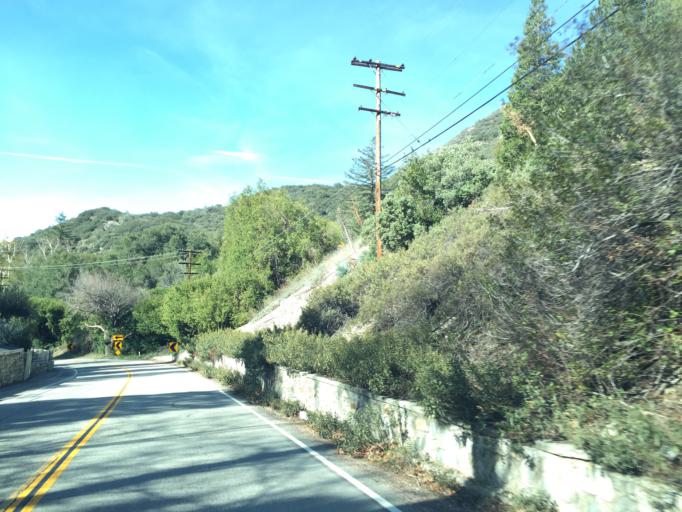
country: US
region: California
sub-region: San Bernardino County
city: San Antonio Heights
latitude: 34.2360
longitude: -117.6606
